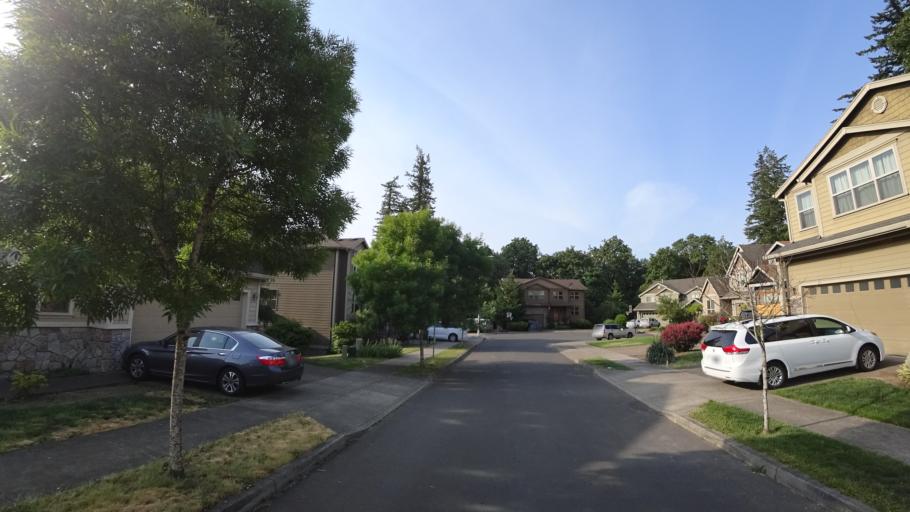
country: US
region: Oregon
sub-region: Clackamas County
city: Happy Valley
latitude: 45.4626
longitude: -122.5124
